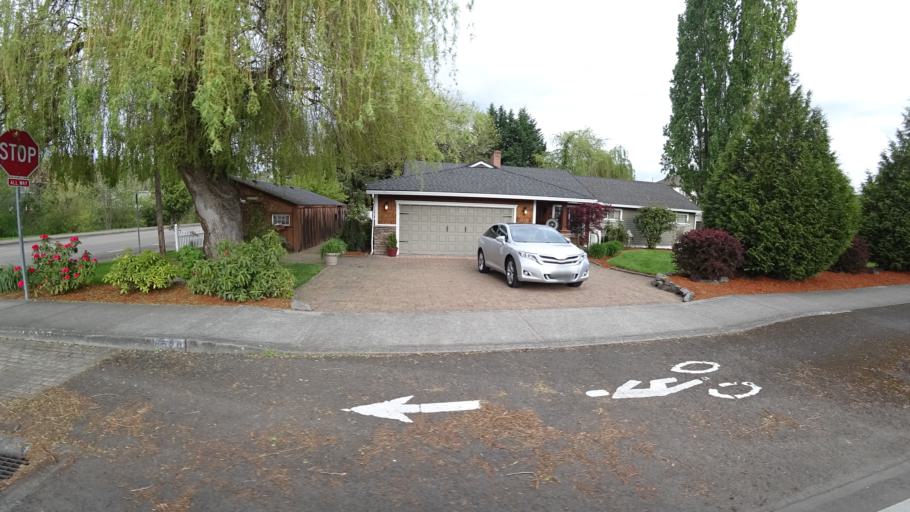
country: US
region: Oregon
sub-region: Washington County
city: Beaverton
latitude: 45.4583
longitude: -122.8363
